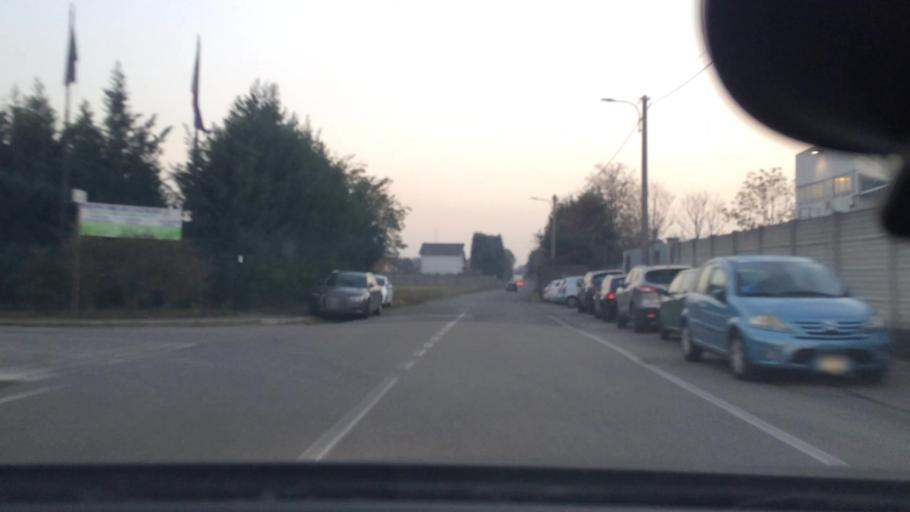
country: IT
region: Lombardy
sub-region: Provincia di Varese
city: Caronno Pertusella
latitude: 45.6067
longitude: 9.0436
